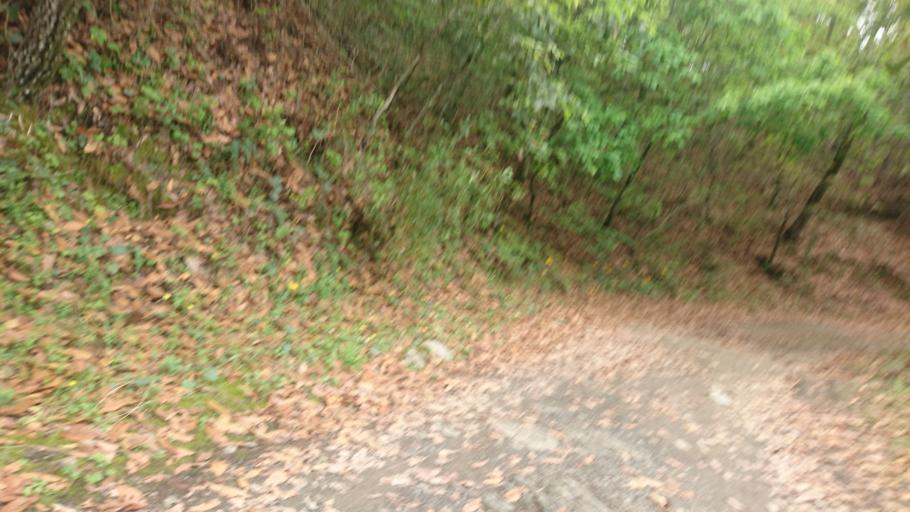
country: MX
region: Nuevo Leon
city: Garza Garcia
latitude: 25.6058
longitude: -100.3432
